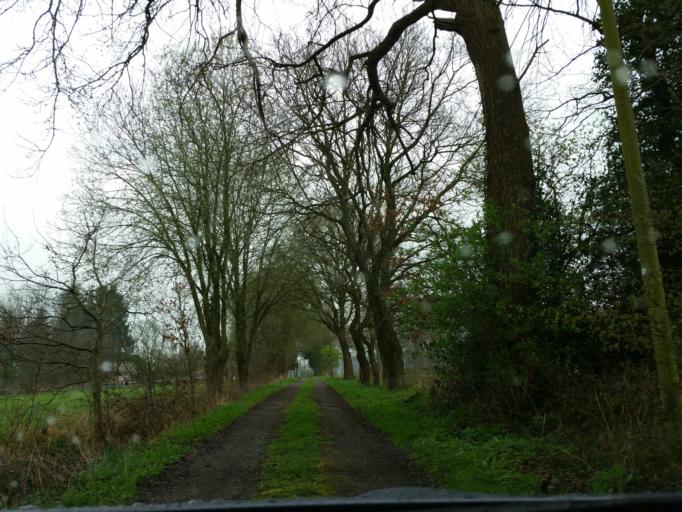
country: DE
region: Lower Saxony
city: Hipstedt
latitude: 53.4732
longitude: 8.9639
